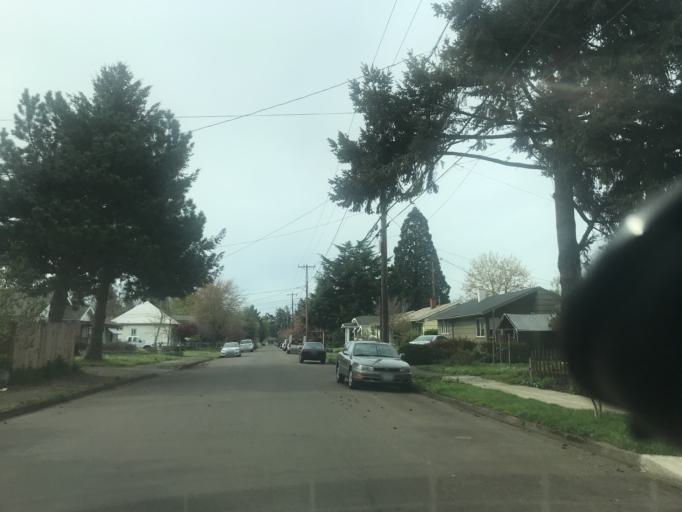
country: US
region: Oregon
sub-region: Multnomah County
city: Lents
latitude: 45.4937
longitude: -122.5847
